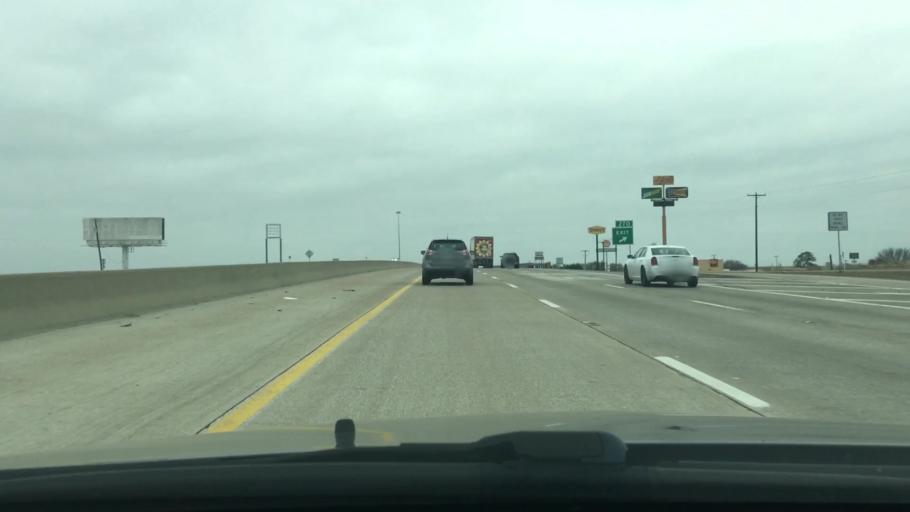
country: US
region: Texas
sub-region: Dallas County
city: Wilmer
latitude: 32.5949
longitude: -96.6812
